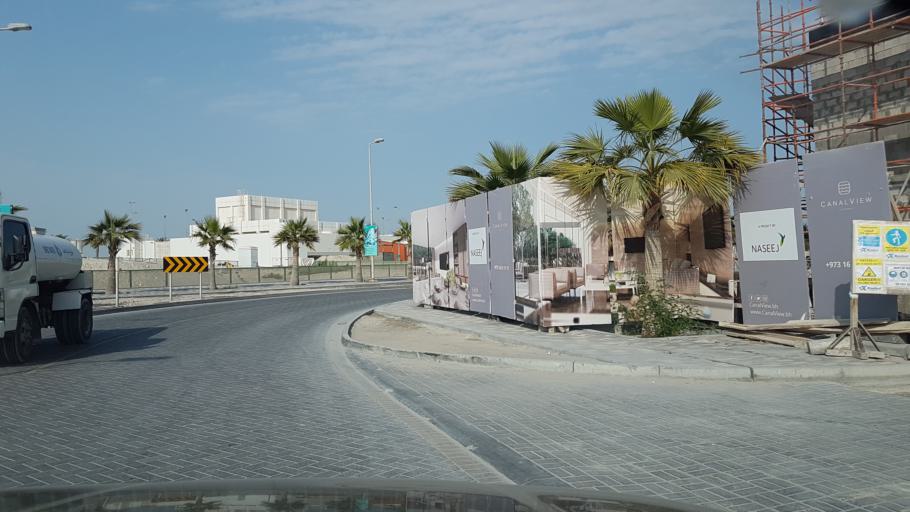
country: BH
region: Muharraq
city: Al Hadd
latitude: 26.2696
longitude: 50.6675
